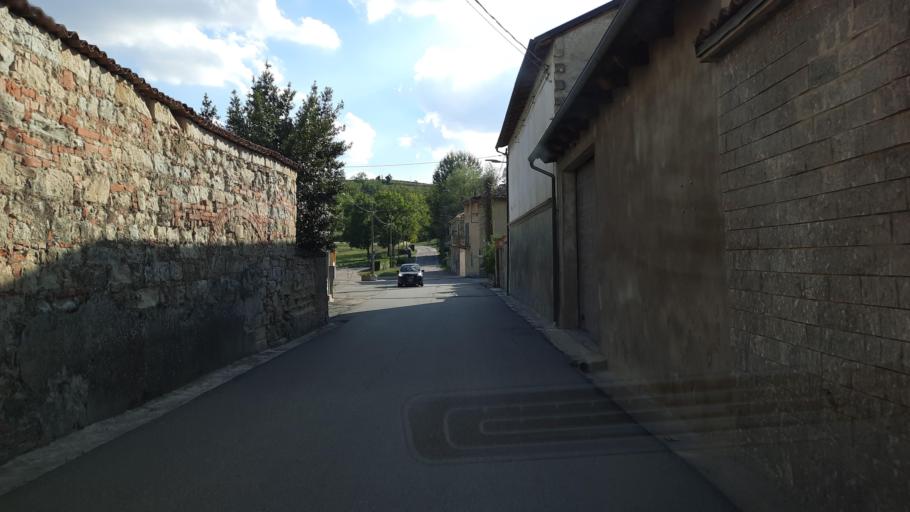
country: IT
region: Piedmont
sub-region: Provincia di Alessandria
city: Ottiglio
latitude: 45.0513
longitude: 8.3370
